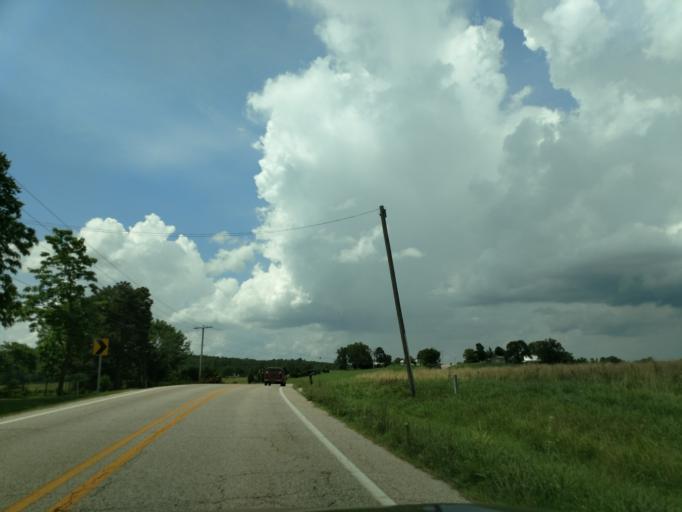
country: US
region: Arkansas
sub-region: Boone County
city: Harrison
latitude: 36.2733
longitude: -93.2343
